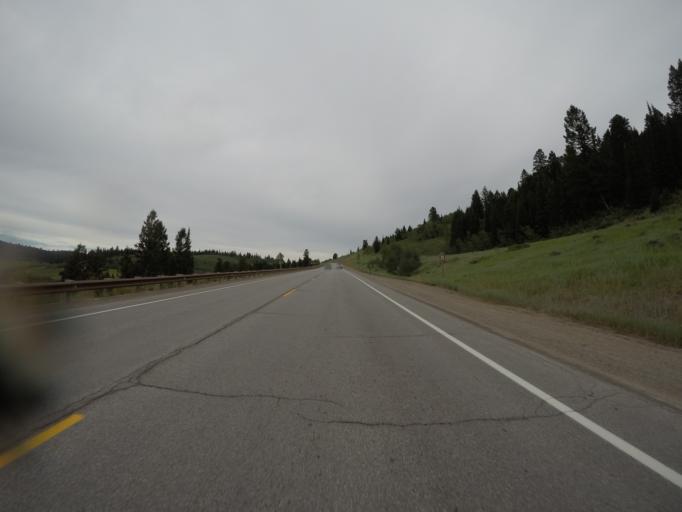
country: US
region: Wyoming
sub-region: Lincoln County
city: Afton
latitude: 42.4969
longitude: -110.9102
